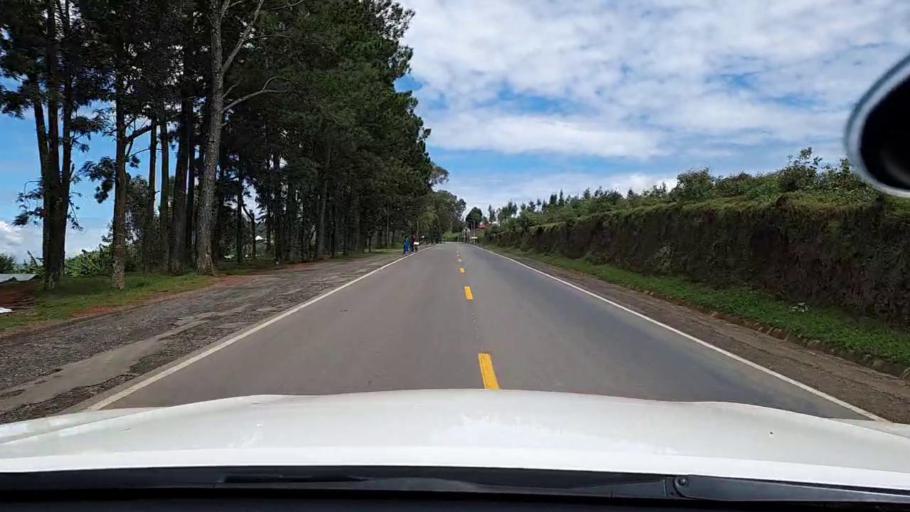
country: RW
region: Kigali
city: Kigali
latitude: -1.8412
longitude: 29.9549
